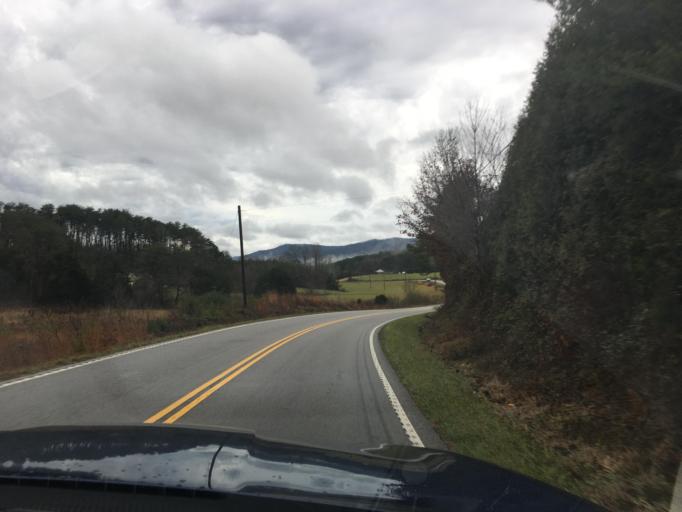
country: US
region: Tennessee
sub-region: McMinn County
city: Englewood
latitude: 35.3560
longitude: -84.3413
